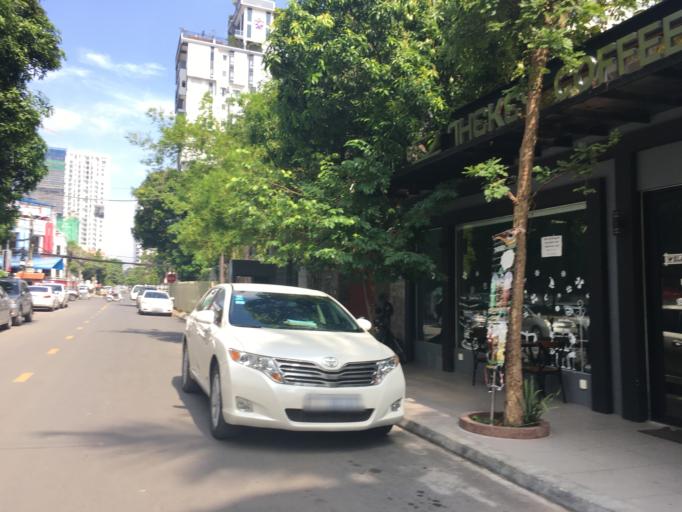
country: KH
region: Phnom Penh
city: Phnom Penh
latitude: 11.5497
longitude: 104.9277
